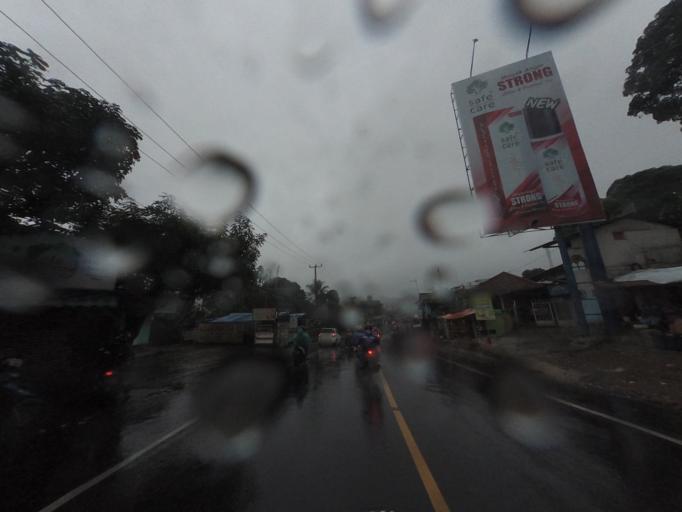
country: ID
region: West Java
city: Caringin
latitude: -6.6538
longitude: 106.8652
